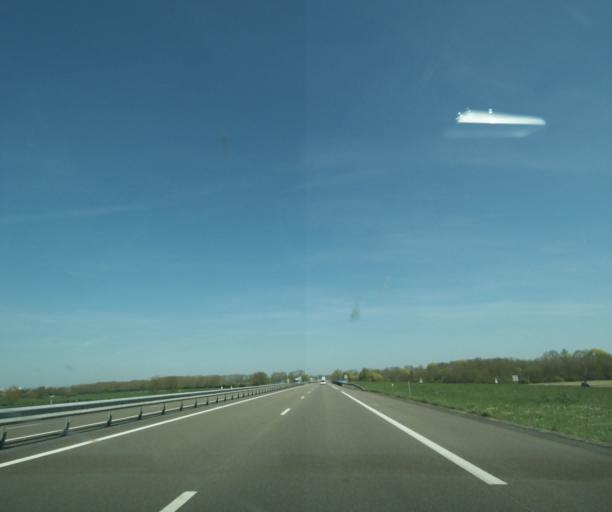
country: FR
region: Bourgogne
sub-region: Departement de la Nievre
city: Sermoise-sur-Loire
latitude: 46.9558
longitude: 3.1720
